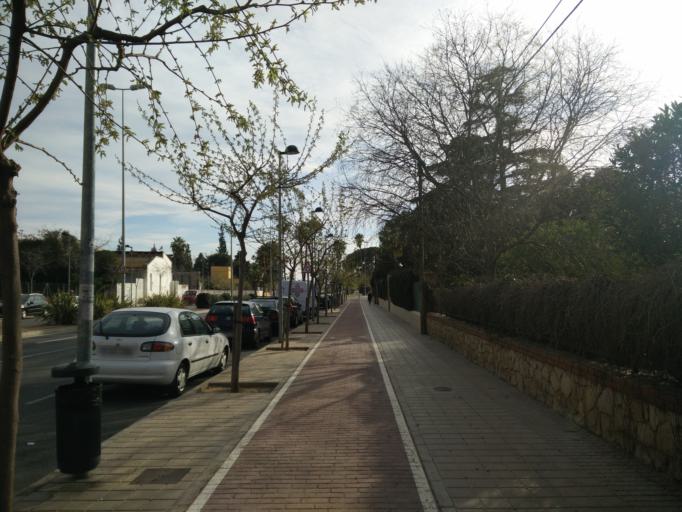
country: ES
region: Valencia
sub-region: Provincia de Castello
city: Castello de la Plana
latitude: 39.9833
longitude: -0.0515
